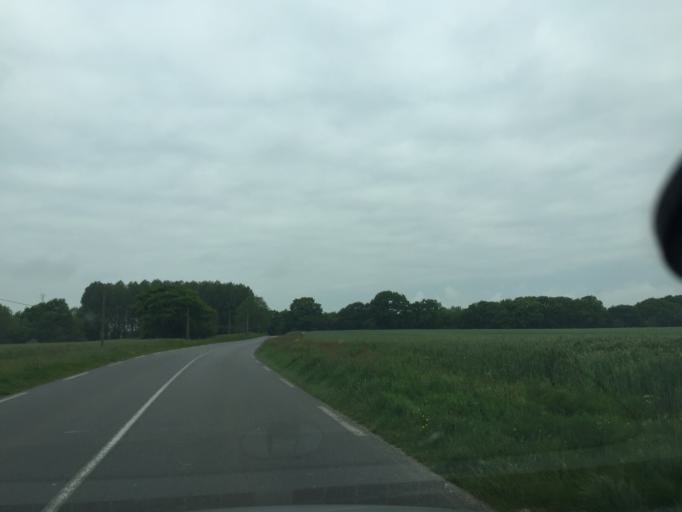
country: FR
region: Brittany
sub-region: Departement des Cotes-d'Armor
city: Henanbihen
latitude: 48.5776
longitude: -2.3435
